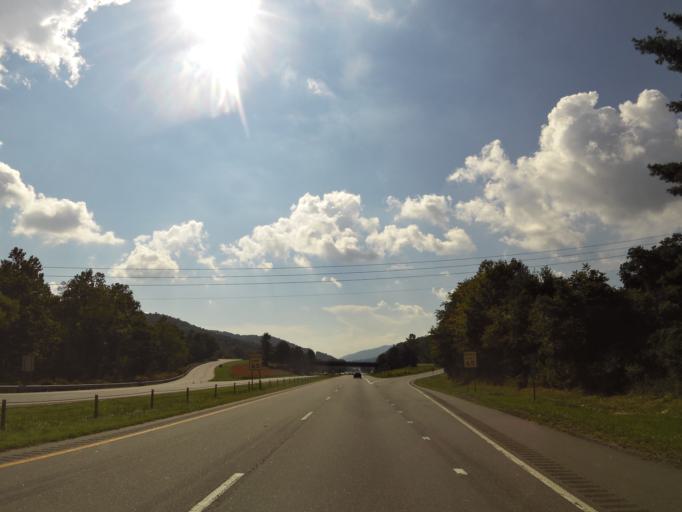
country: US
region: North Carolina
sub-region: Buncombe County
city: Black Mountain
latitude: 35.6193
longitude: -82.2835
